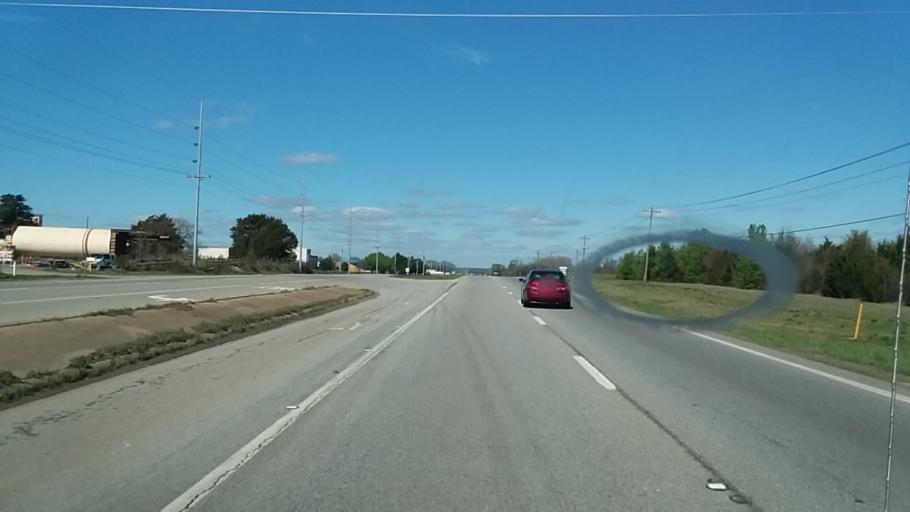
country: US
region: Alabama
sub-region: Morgan County
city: Trinity
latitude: 34.6224
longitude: -87.0797
